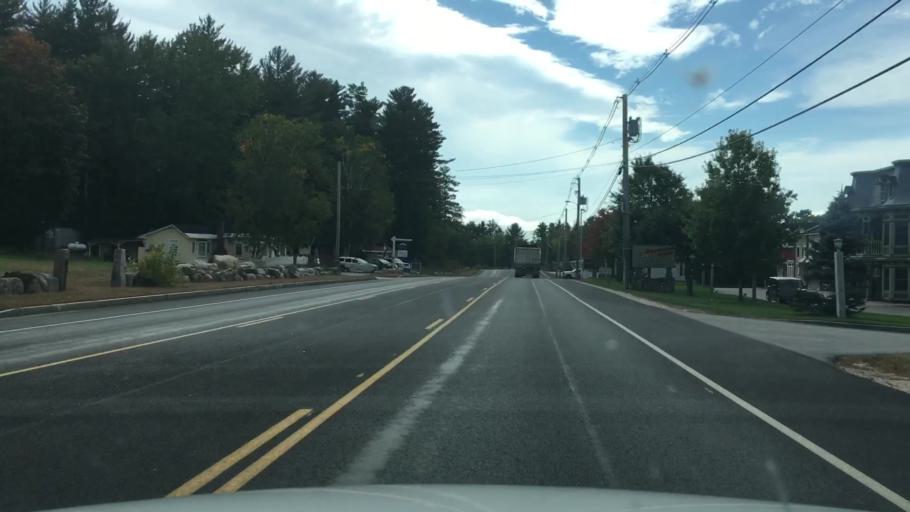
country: US
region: New Hampshire
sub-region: Carroll County
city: North Conway
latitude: 44.0707
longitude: -71.1428
